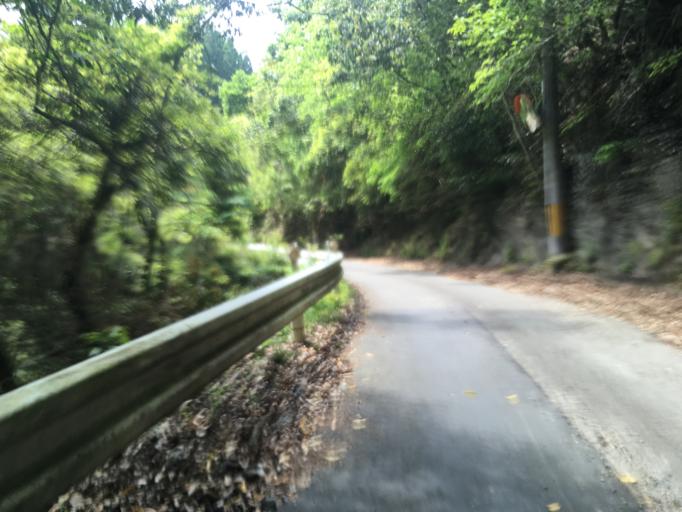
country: JP
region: Kyoto
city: Kameoka
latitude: 35.0291
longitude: 135.6365
